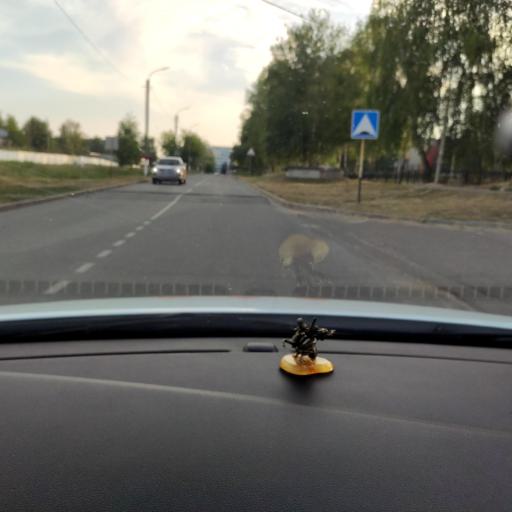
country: RU
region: Tatarstan
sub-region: Zelenodol'skiy Rayon
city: Zelenodolsk
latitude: 55.8563
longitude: 48.5696
